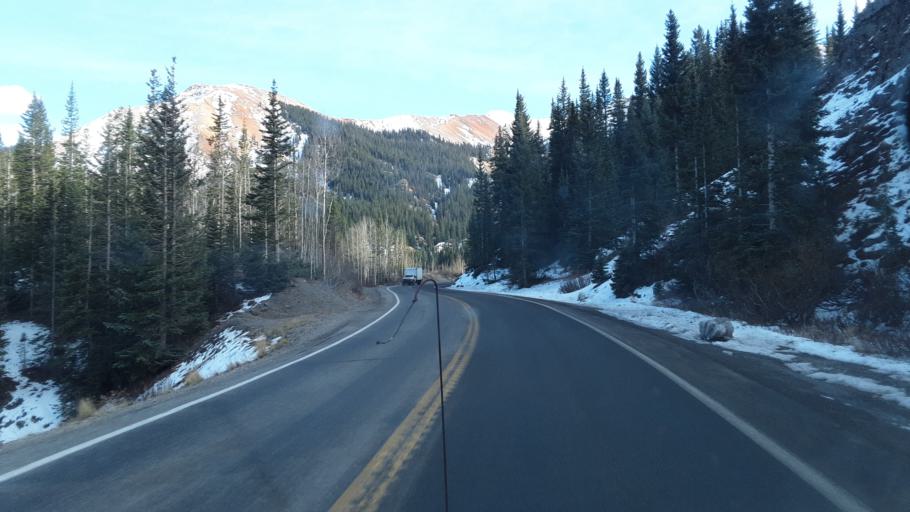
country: US
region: Colorado
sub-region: Ouray County
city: Ouray
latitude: 37.9188
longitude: -107.7008
